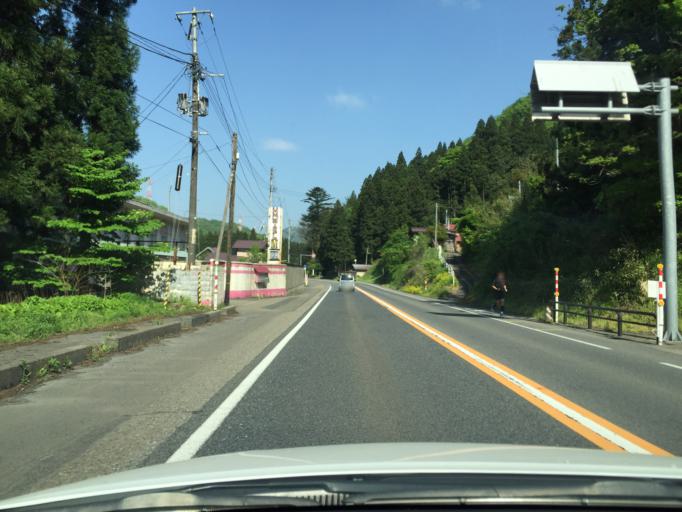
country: JP
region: Niigata
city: Suibara
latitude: 37.7319
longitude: 139.3332
